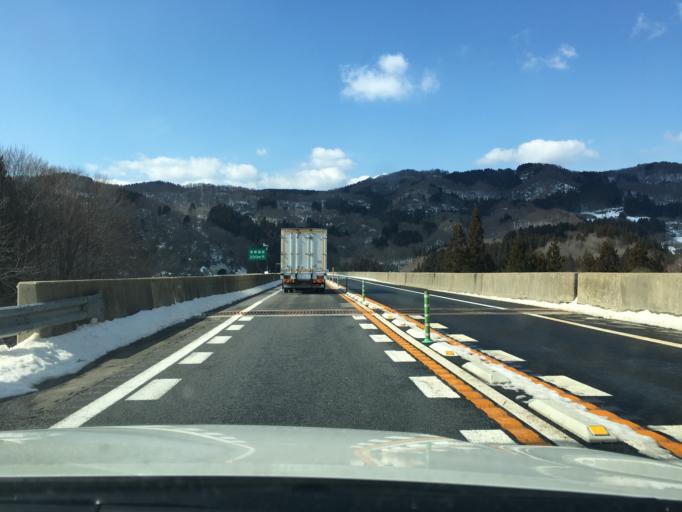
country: JP
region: Yamagata
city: Tsuruoka
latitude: 38.5907
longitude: 139.8880
